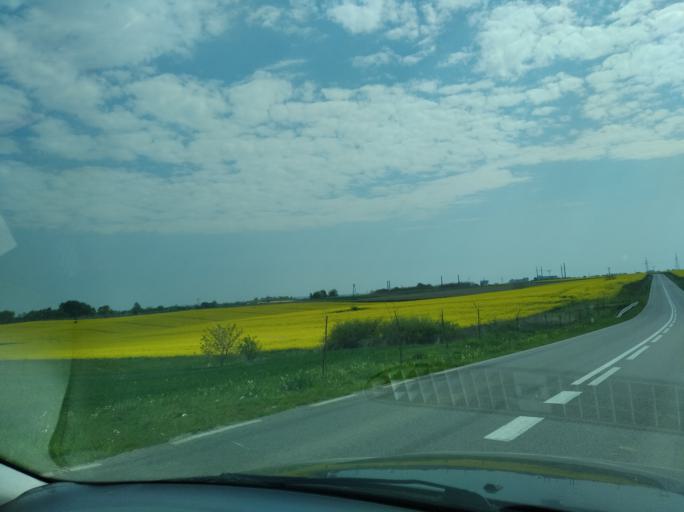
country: PL
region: Subcarpathian Voivodeship
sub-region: Powiat jaroslawski
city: Jaroslaw
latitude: 49.9973
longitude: 22.6805
